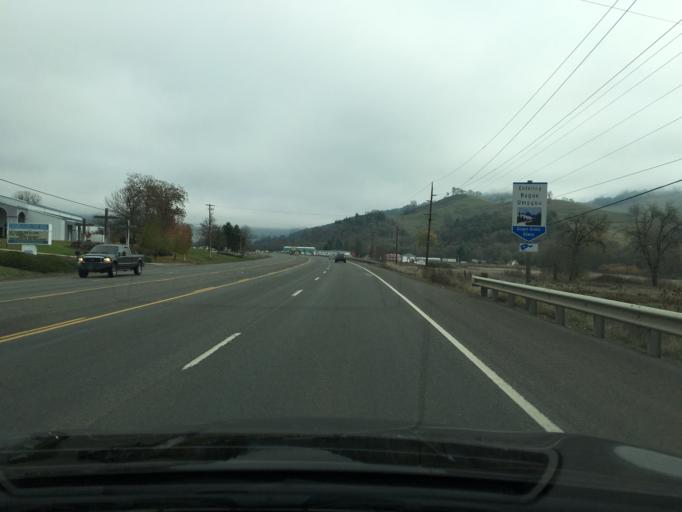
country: US
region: Oregon
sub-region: Douglas County
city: Roseburg
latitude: 43.2129
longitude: -123.3072
